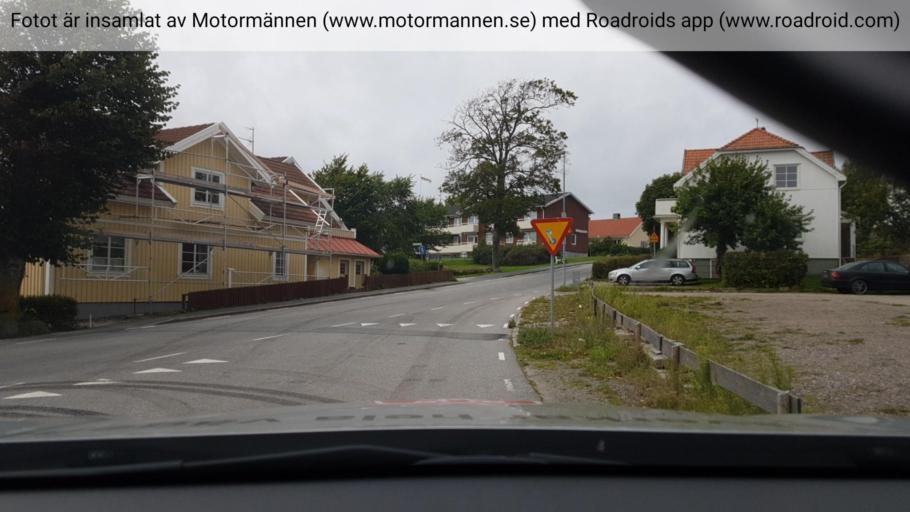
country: SE
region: Vaestra Goetaland
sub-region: Tanums Kommun
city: Grebbestad
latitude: 58.6930
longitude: 11.2554
